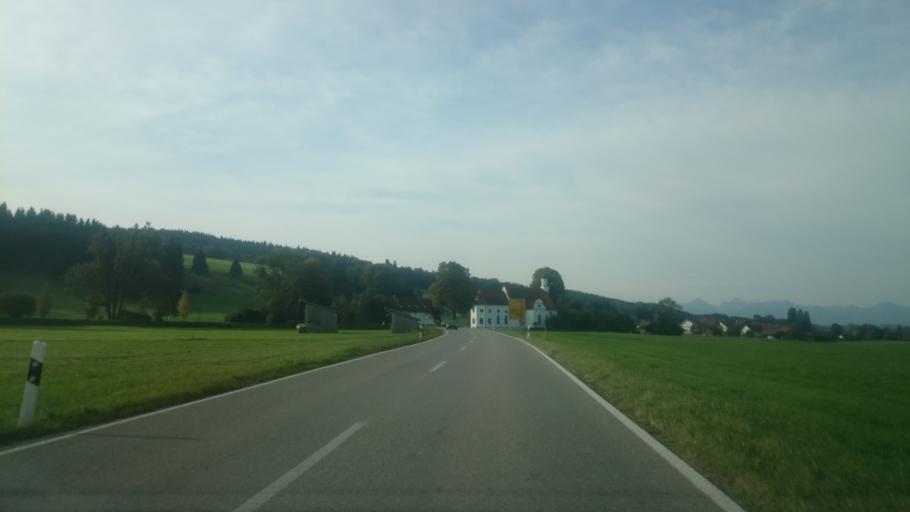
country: DE
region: Bavaria
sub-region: Upper Bavaria
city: Steingaden
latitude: 47.7225
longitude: 10.8900
